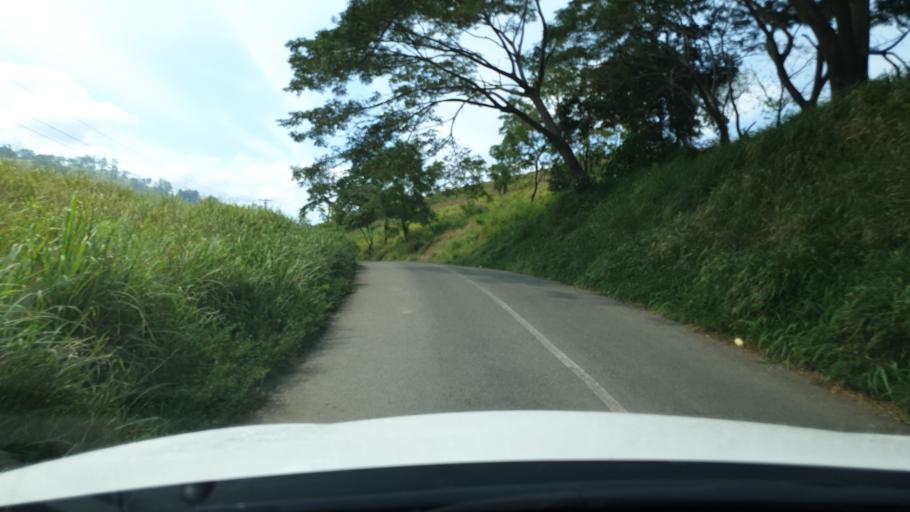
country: PG
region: Central Province
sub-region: Rigo
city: Kwikila
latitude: -9.8322
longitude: 147.5624
